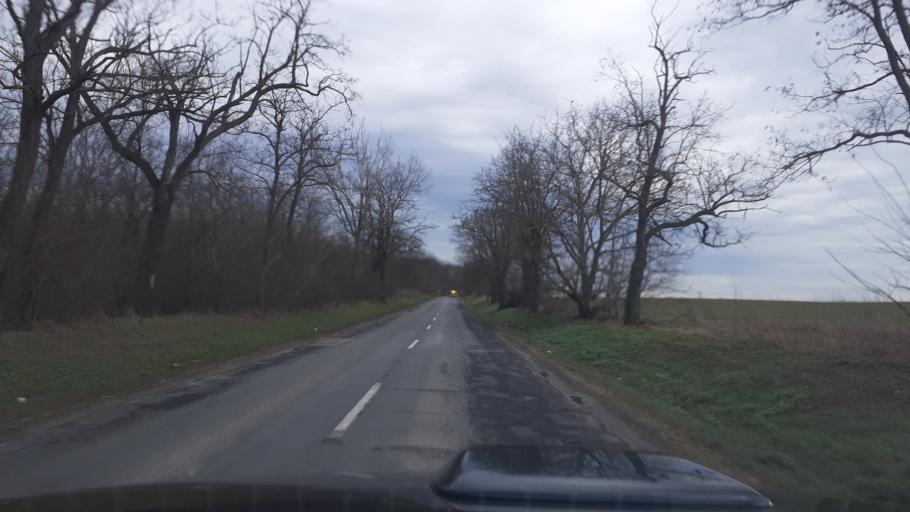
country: HU
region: Fejer
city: Sarosd
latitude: 47.0260
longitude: 18.6706
